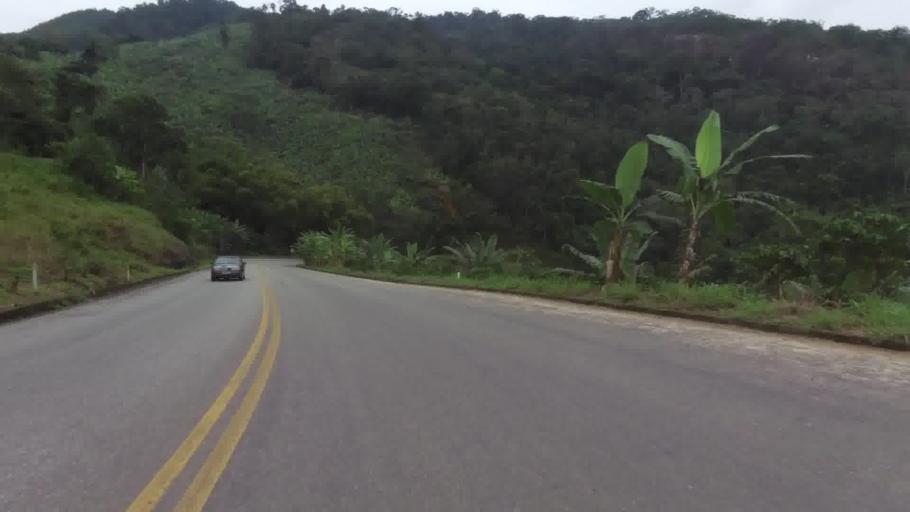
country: BR
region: Espirito Santo
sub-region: Iconha
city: Iconha
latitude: -20.7844
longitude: -40.8136
